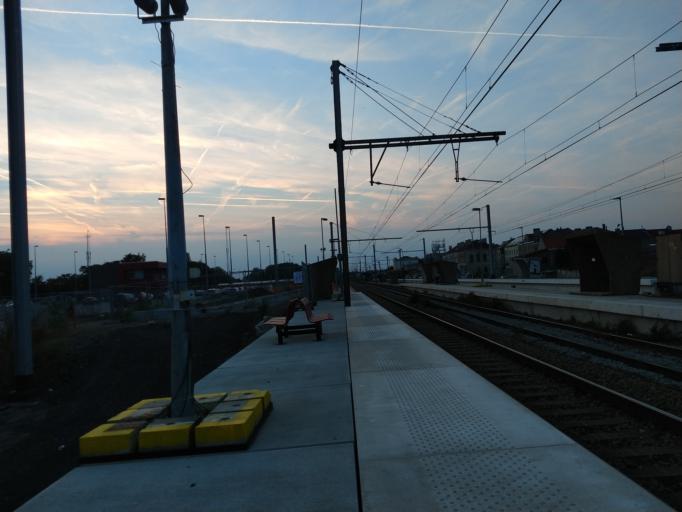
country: BE
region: Flanders
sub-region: Provincie Vlaams-Brabant
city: Tienen
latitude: 50.8060
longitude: 4.9283
